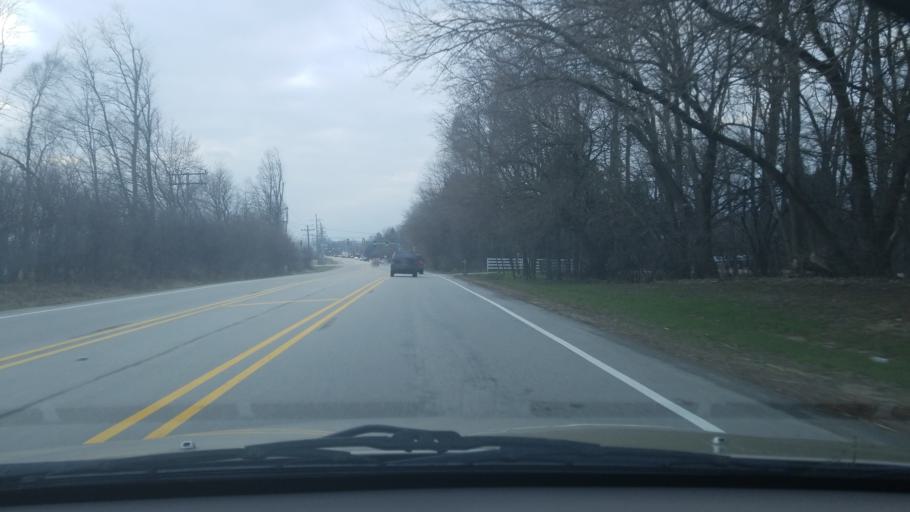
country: US
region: Illinois
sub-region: Kane County
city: Carpentersville
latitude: 42.1541
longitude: -88.2553
